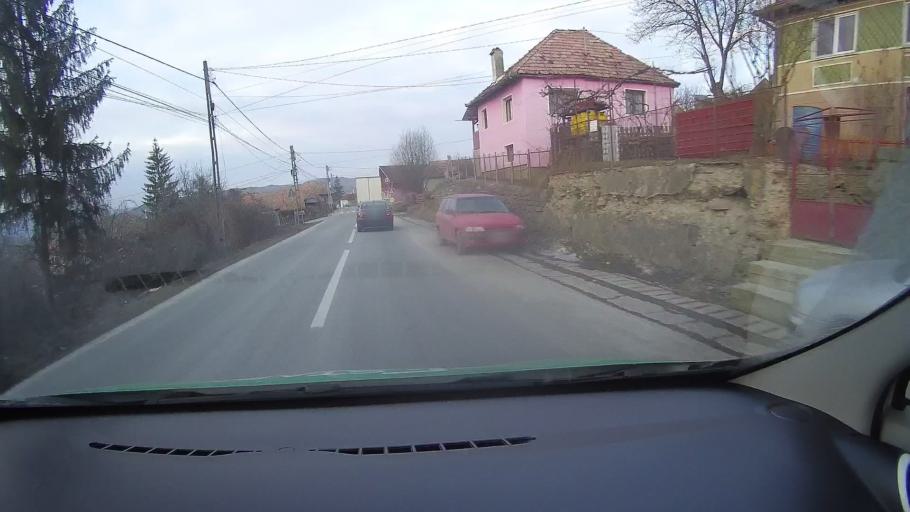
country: RO
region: Harghita
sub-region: Comuna Simonesti
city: Simonesti
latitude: 46.3317
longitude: 25.1059
